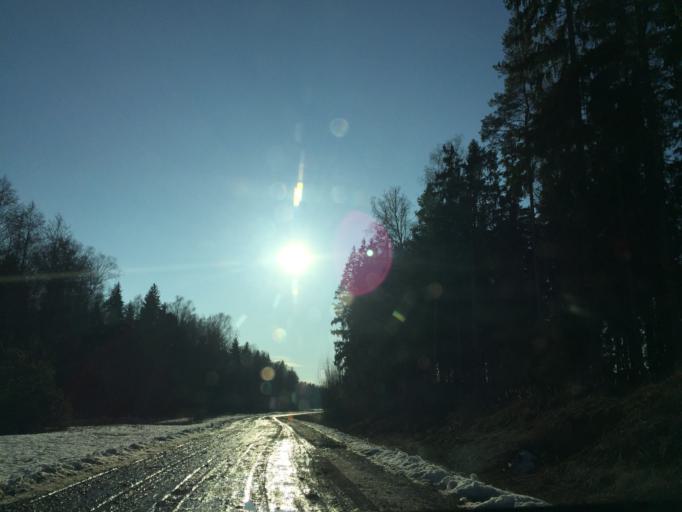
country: LV
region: Lecava
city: Iecava
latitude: 56.6900
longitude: 24.0782
